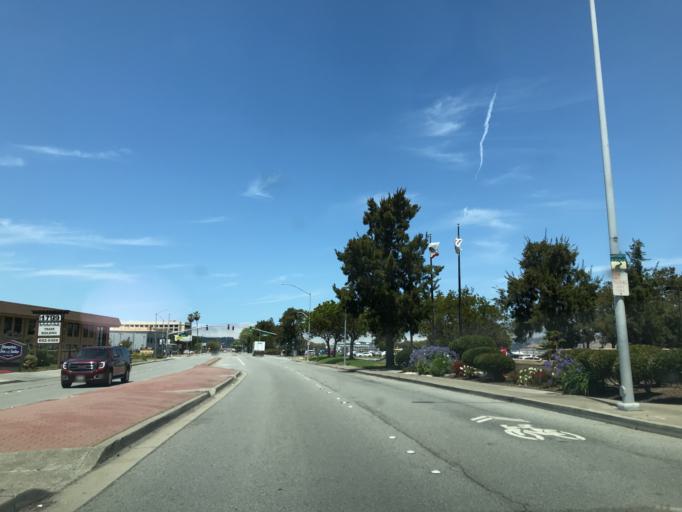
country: US
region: California
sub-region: San Mateo County
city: Millbrae
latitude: 37.6020
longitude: -122.3708
